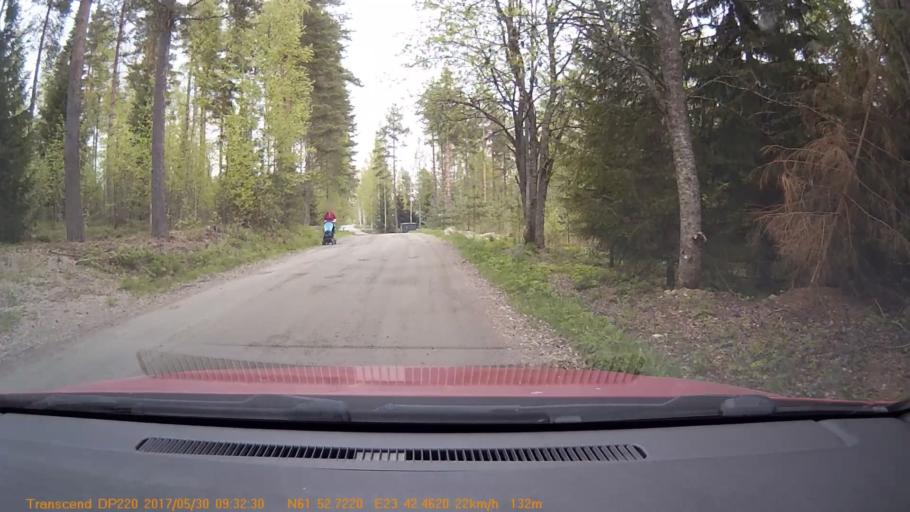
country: FI
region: Pirkanmaa
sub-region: Tampere
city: Kuru
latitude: 61.8787
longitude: 23.7076
